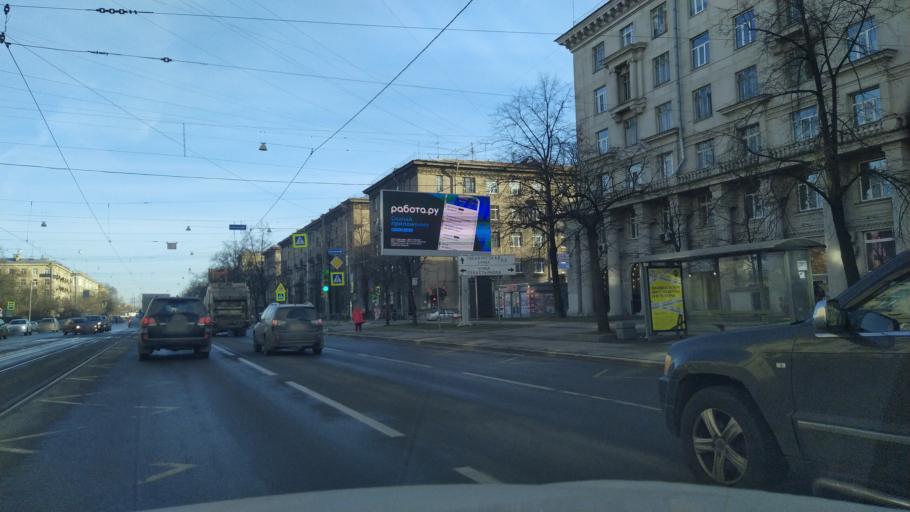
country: RU
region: St.-Petersburg
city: Kupchino
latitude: 59.8760
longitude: 30.3272
